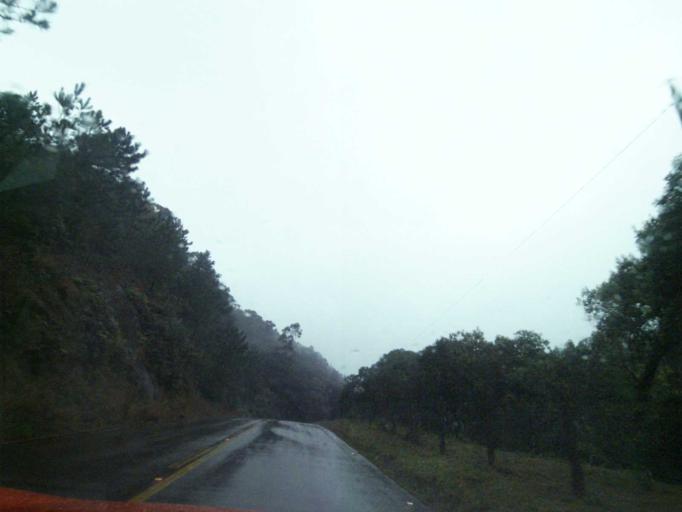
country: BR
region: Santa Catarina
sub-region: Anitapolis
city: Anitapolis
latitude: -27.8286
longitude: -49.0507
